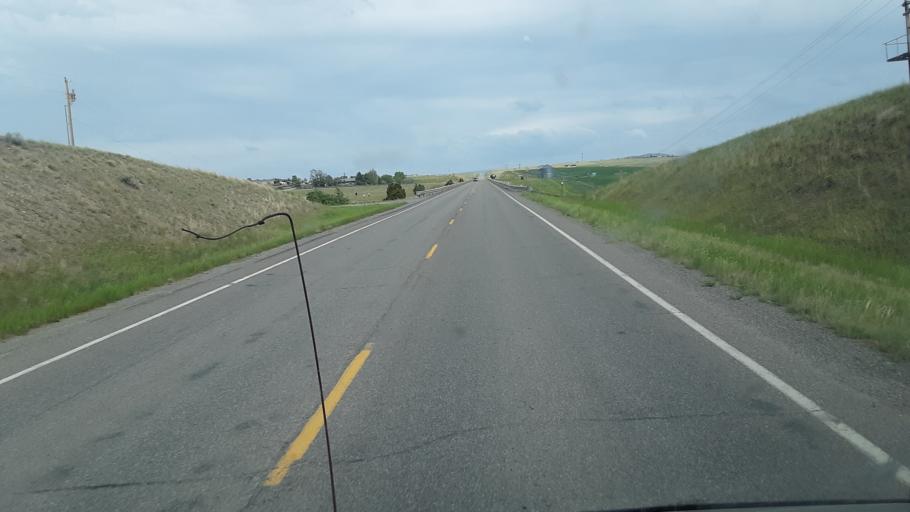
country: US
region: Montana
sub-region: Broadwater County
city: Townsend
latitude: 46.3211
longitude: -111.4577
